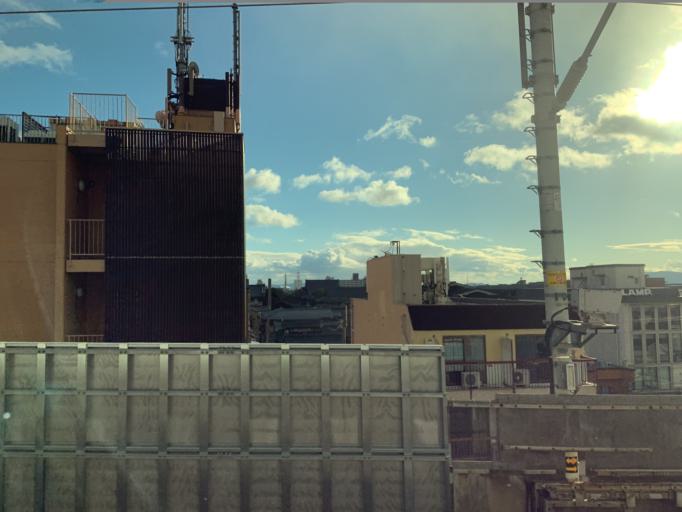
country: JP
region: Kyoto
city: Kyoto
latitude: 34.9847
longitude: 135.7480
